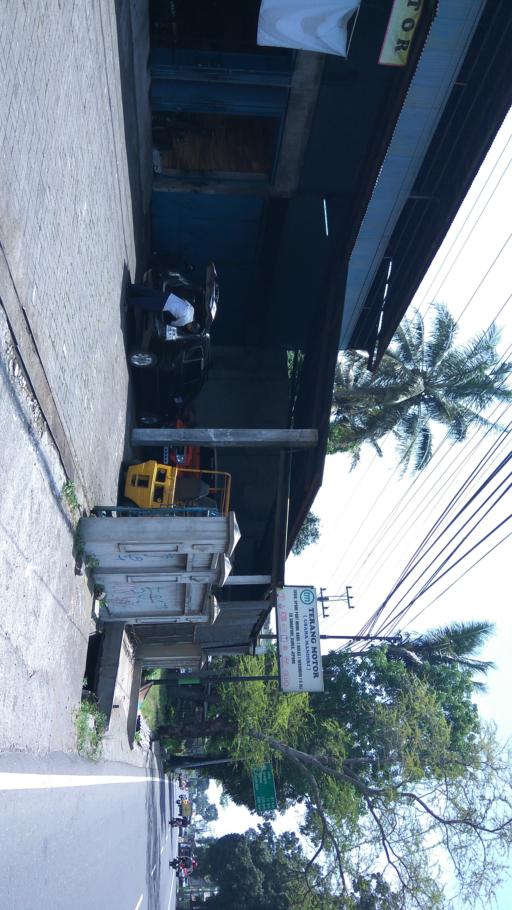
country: ID
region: Central Java
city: Salatiga
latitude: -7.3701
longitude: 110.5148
